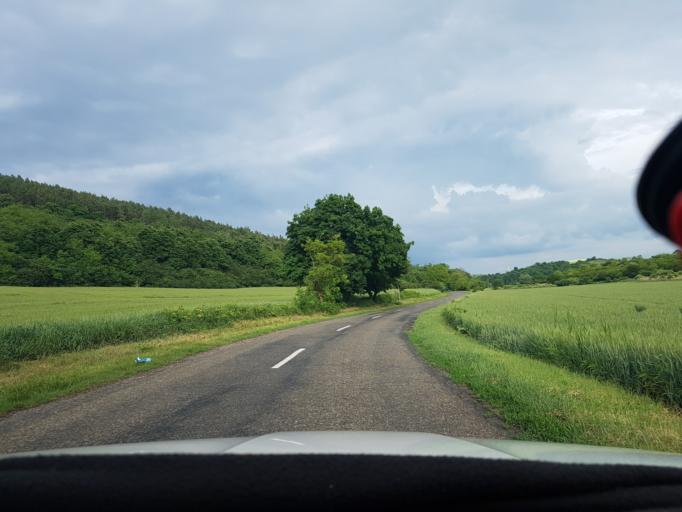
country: HU
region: Komarom-Esztergom
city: Bajna
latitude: 47.7047
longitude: 18.6091
